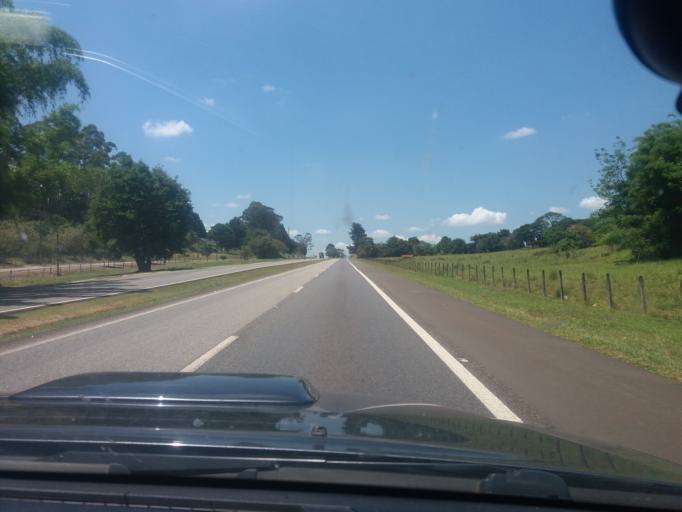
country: BR
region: Sao Paulo
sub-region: Tatui
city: Tatui
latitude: -23.3902
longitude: -47.9247
